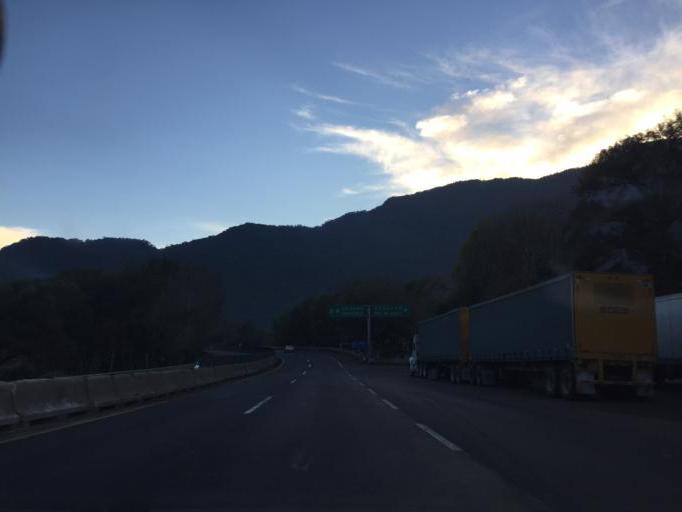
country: MX
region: Veracruz
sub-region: Huiloapan de Cuauhtemoc
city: Huiloapan de Cuauhtemoc
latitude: 18.8196
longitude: -97.1637
